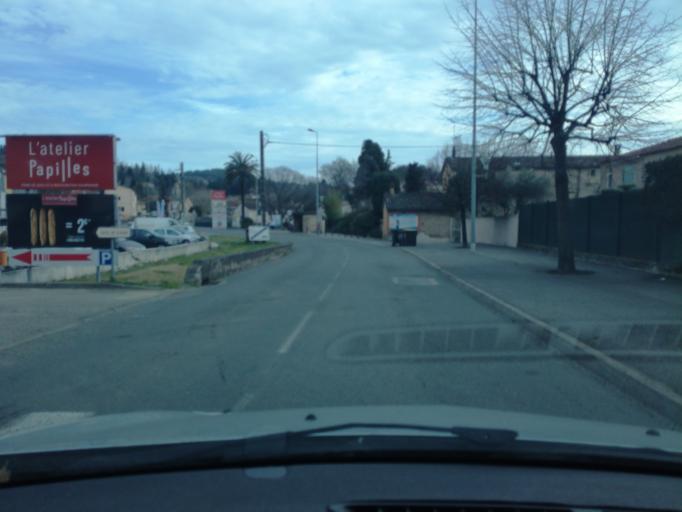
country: FR
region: Provence-Alpes-Cote d'Azur
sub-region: Departement des Alpes-Maritimes
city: Mouans-Sartoux
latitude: 43.6434
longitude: 6.9557
